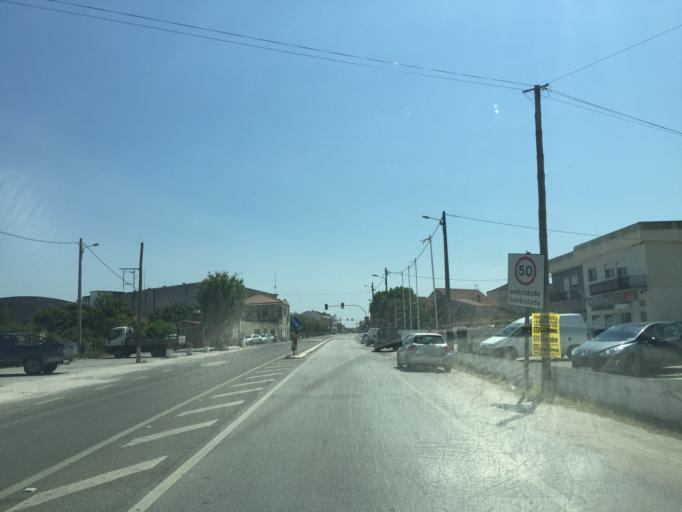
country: PT
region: Coimbra
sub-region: Montemor-O-Velho
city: Arazede
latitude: 40.3176
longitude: -8.7528
